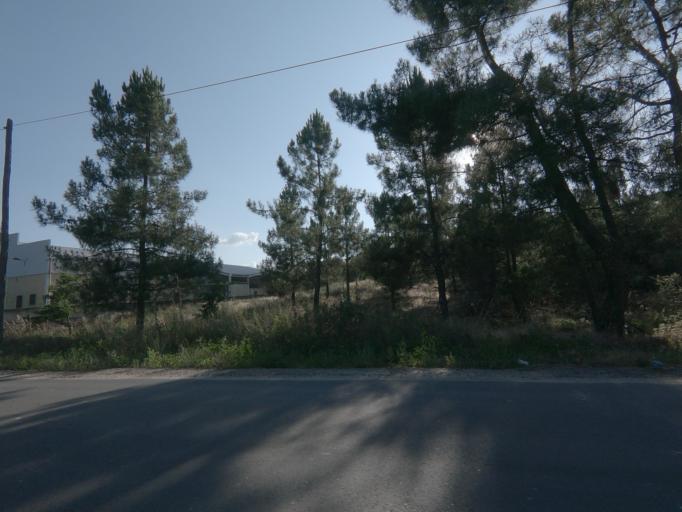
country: PT
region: Vila Real
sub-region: Chaves
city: Chaves
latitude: 41.7910
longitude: -7.4331
